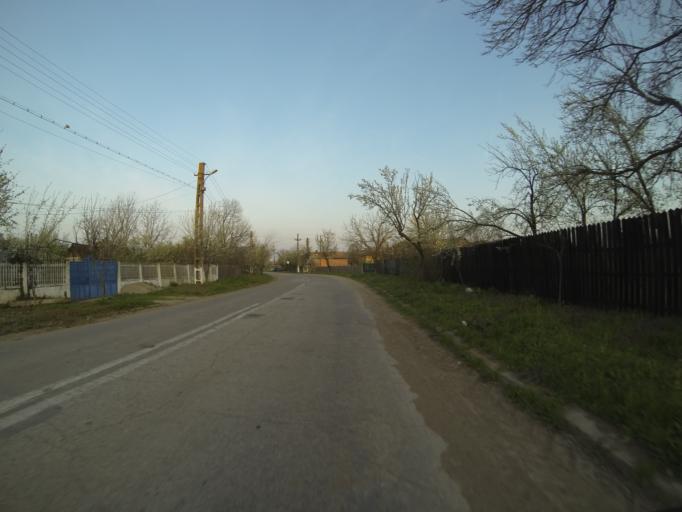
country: RO
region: Dolj
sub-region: Comuna Dranicu
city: Dranic
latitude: 44.0563
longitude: 23.8371
